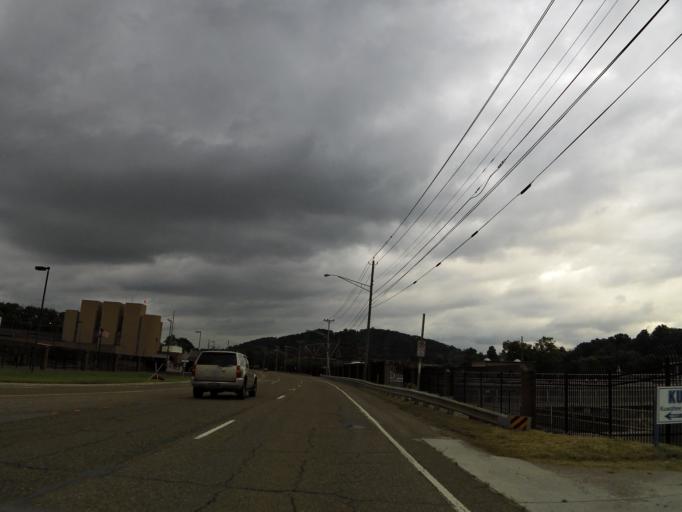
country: US
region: Tennessee
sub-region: Knox County
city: Knoxville
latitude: 35.9444
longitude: -83.9295
